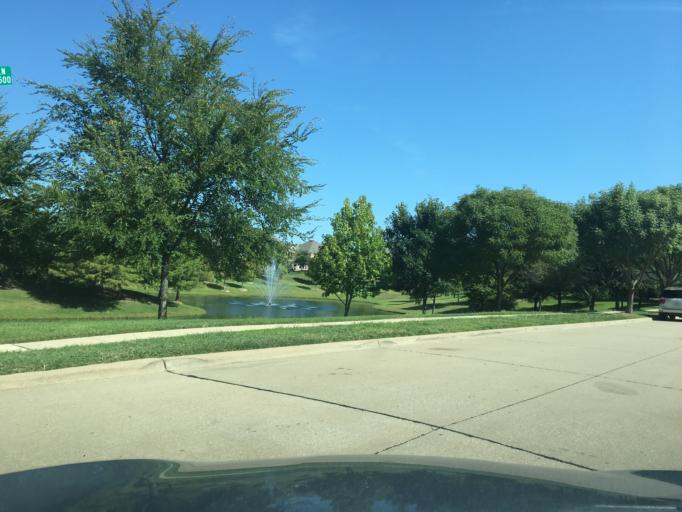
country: US
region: Texas
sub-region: Dallas County
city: Sachse
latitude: 32.9649
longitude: -96.6053
